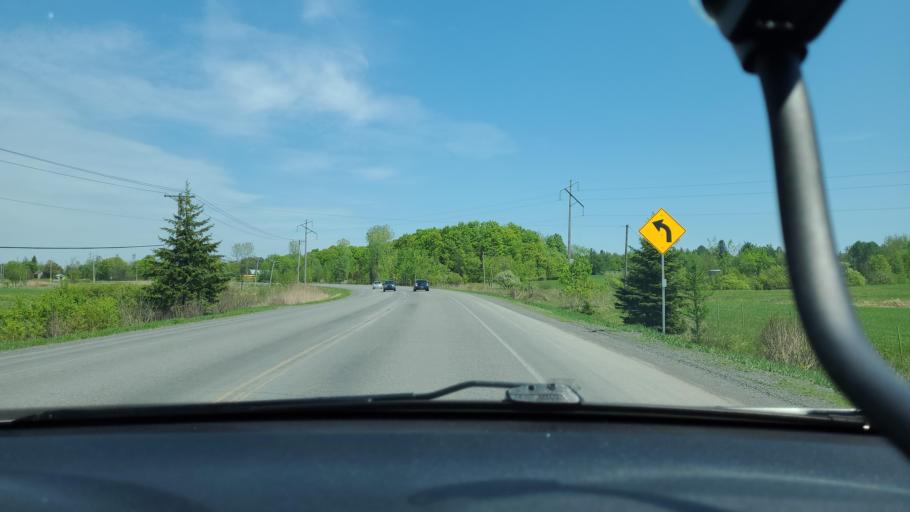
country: CA
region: Quebec
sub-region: Laurentides
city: Saint-Colomban
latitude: 45.6688
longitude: -74.2116
